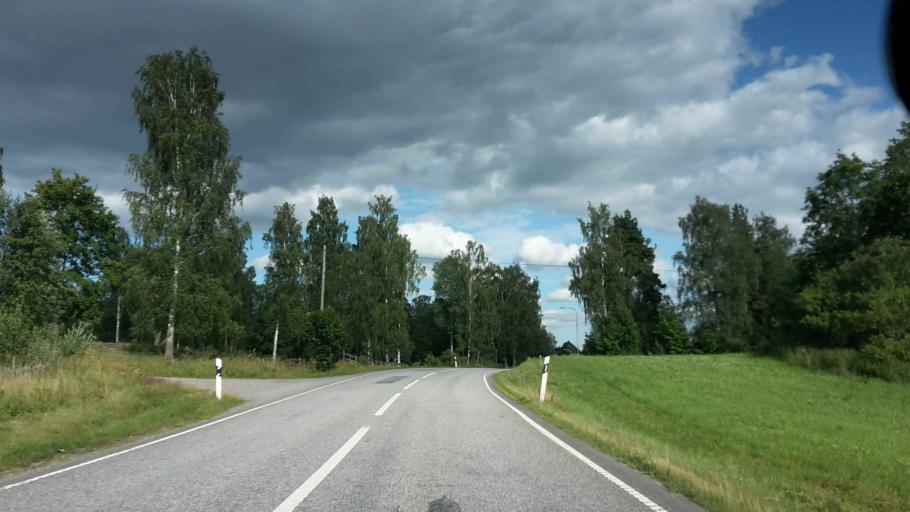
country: SE
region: OEstergoetland
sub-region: Linkopings Kommun
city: Ljungsbro
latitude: 58.7913
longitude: 15.4688
